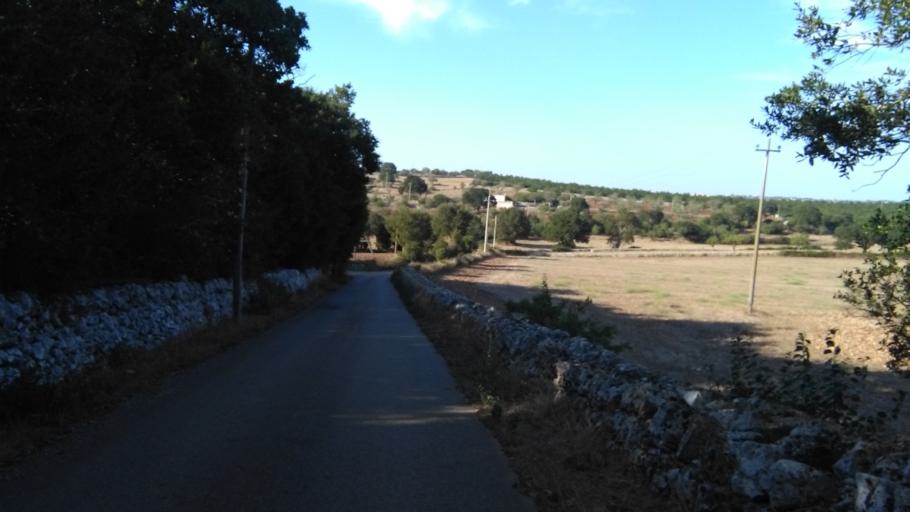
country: IT
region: Apulia
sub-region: Provincia di Bari
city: Putignano
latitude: 40.8274
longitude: 17.0587
